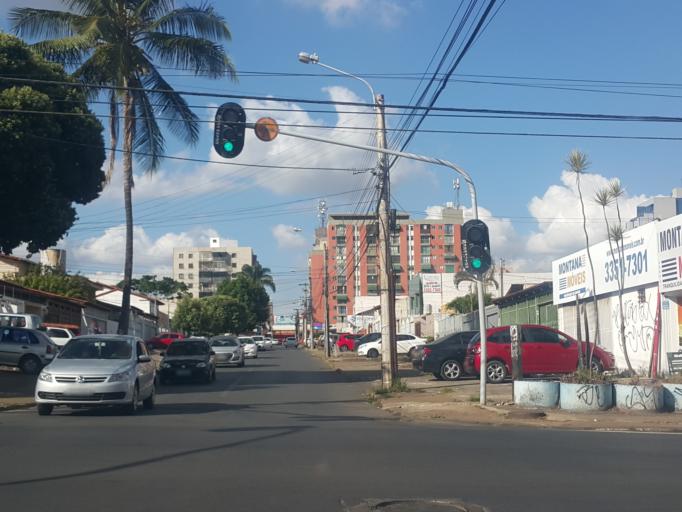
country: BR
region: Federal District
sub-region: Brasilia
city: Brasilia
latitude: -15.8234
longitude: -48.0643
